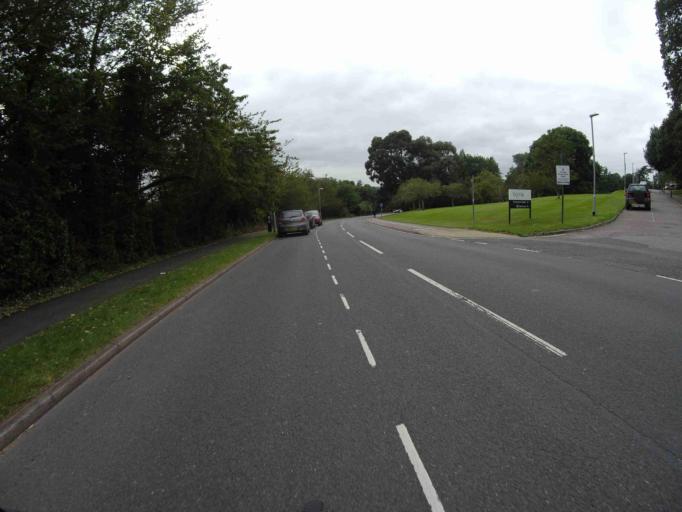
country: GB
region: England
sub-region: Devon
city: Exeter
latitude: 50.7322
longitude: -3.5352
